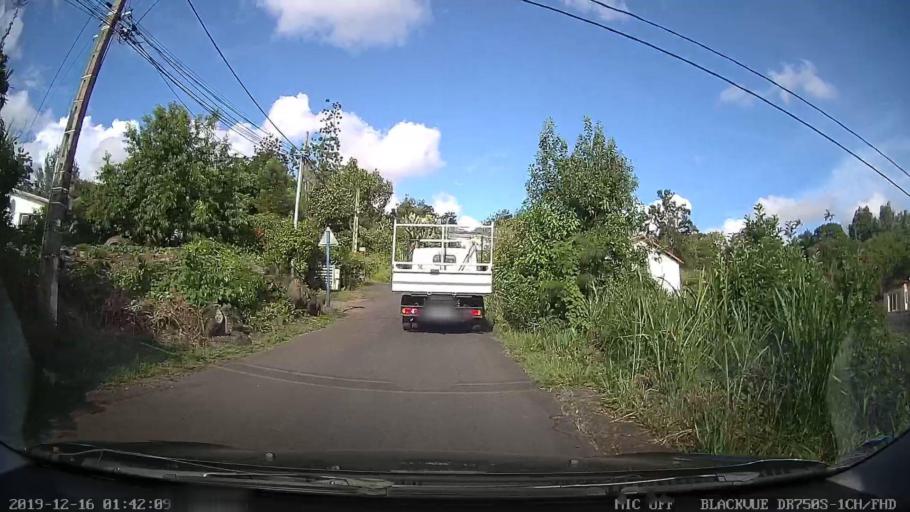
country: RE
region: Reunion
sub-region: Reunion
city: Le Tampon
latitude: -21.2543
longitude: 55.5108
